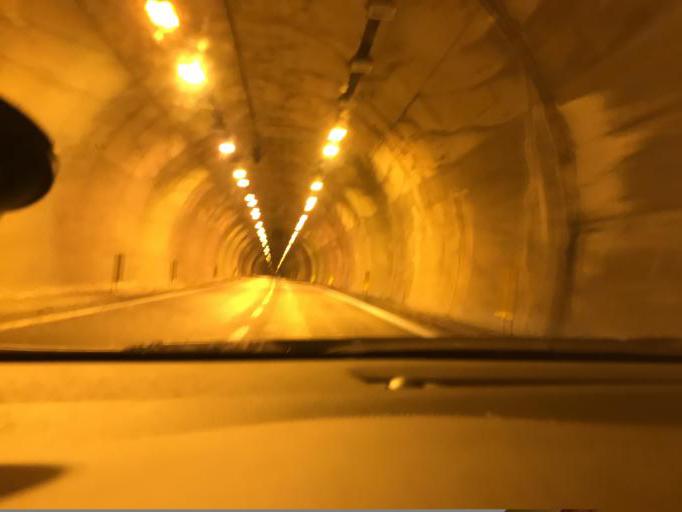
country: IT
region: The Marches
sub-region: Provincia di Ancona
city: Fabriano
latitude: 43.3247
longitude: 12.9050
